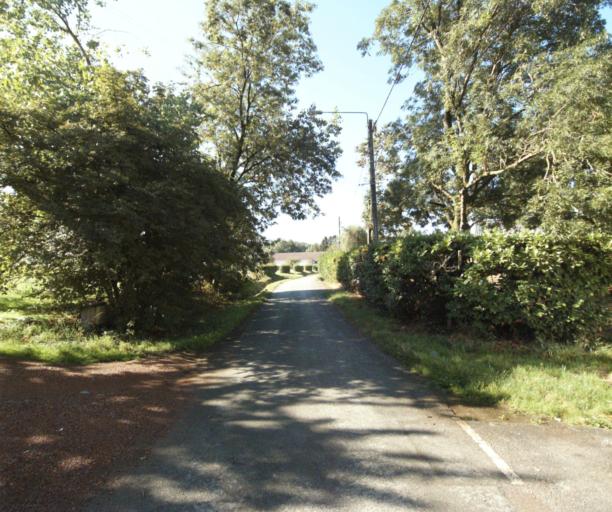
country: FR
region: Nord-Pas-de-Calais
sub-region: Departement du Nord
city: Willems
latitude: 50.6445
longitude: 3.2426
